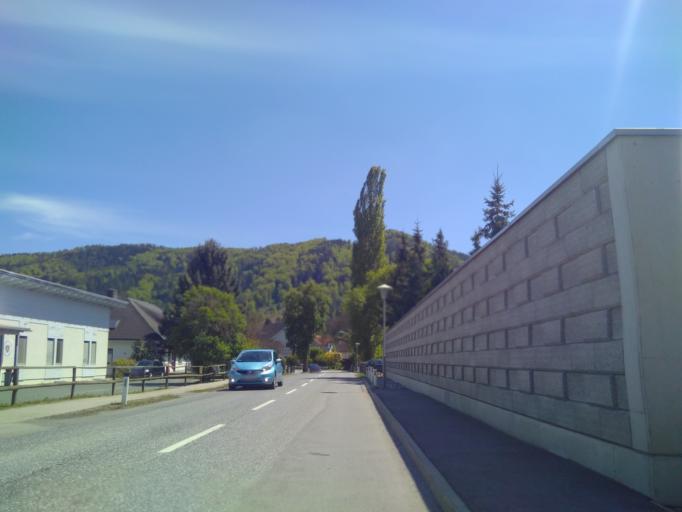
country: AT
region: Styria
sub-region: Politischer Bezirk Graz-Umgebung
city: Gratkorn
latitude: 47.1181
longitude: 15.3393
